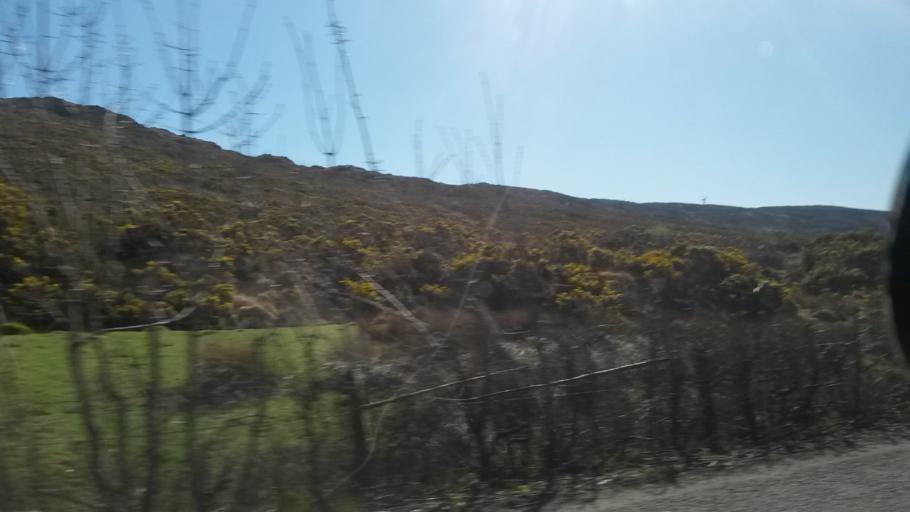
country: IE
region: Munster
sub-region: Ciarrai
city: Cill Airne
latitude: 51.9474
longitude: -9.3884
